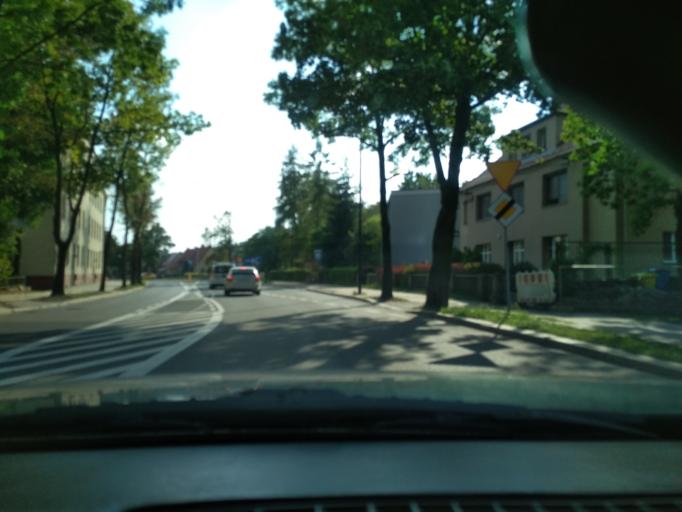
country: PL
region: Silesian Voivodeship
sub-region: Gliwice
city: Gliwice
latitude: 50.2936
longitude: 18.6436
